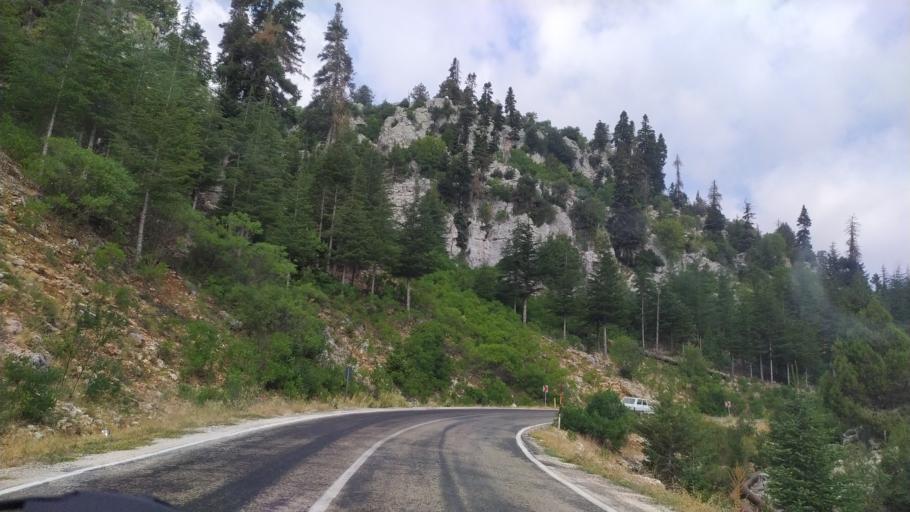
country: TR
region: Mersin
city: Kirobasi
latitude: 36.6043
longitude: 33.8865
